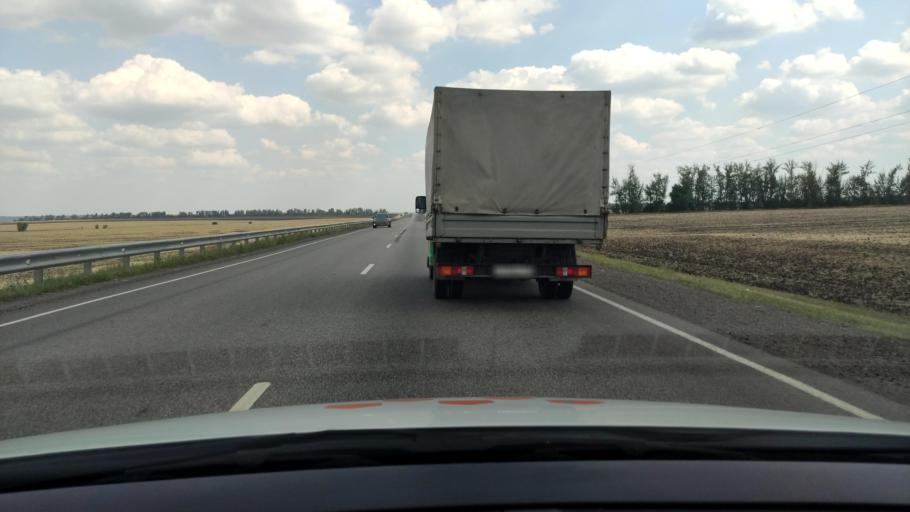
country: RU
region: Voronezj
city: Volya
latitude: 51.6860
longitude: 39.5293
